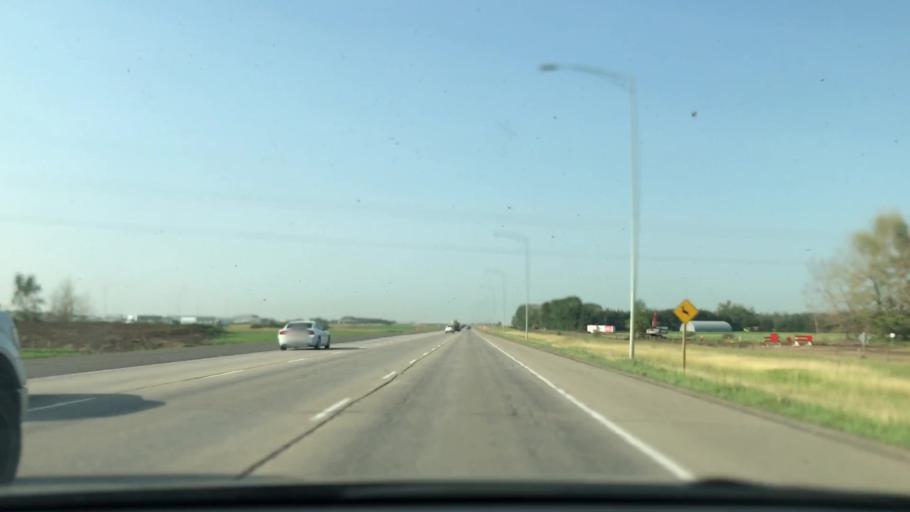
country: CA
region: Alberta
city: Leduc
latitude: 53.3699
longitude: -113.5301
